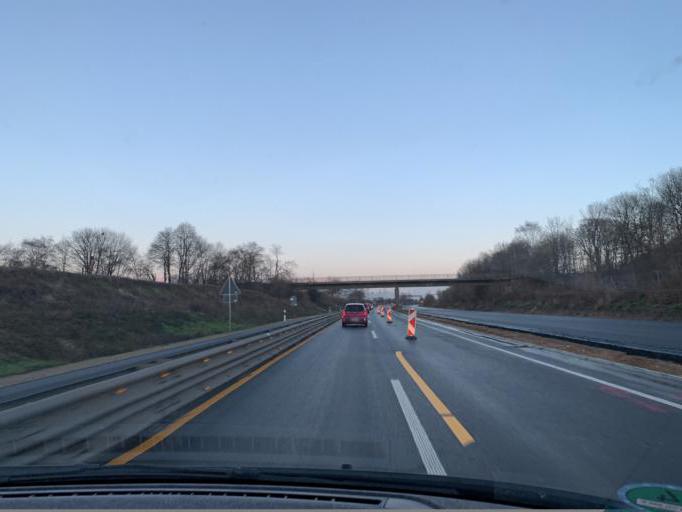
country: DE
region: North Rhine-Westphalia
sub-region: Regierungsbezirk Dusseldorf
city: Grevenbroich
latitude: 51.0749
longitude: 6.6117
